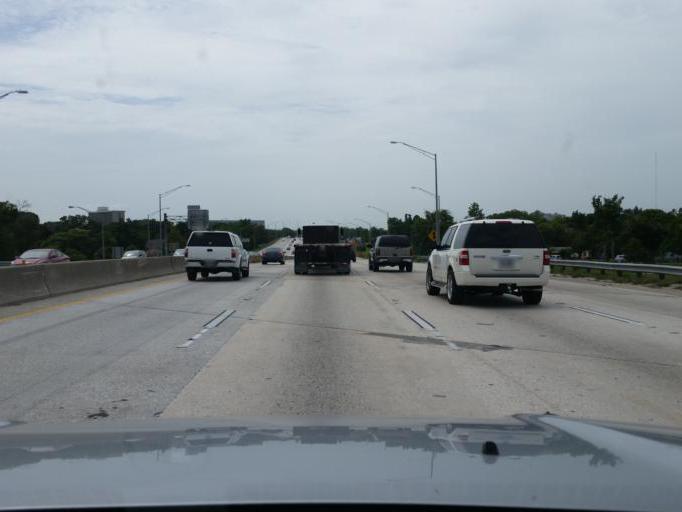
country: US
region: Florida
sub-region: Orange County
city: Fairview Shores
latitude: 28.5930
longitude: -81.3821
